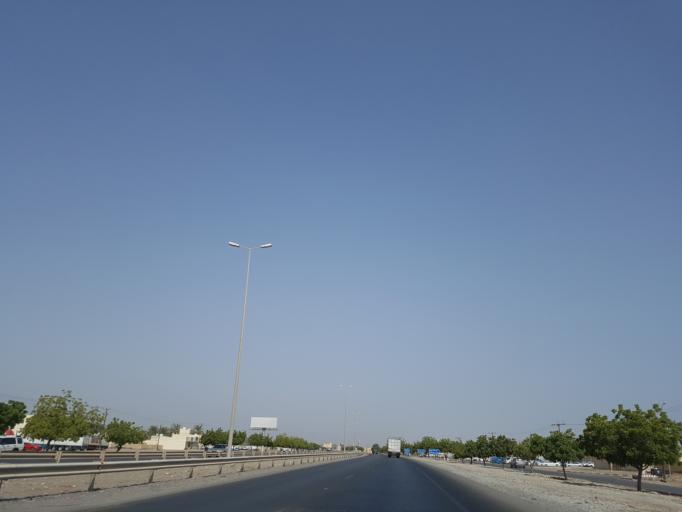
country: OM
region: Al Batinah
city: As Suwayq
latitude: 23.7528
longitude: 57.6104
